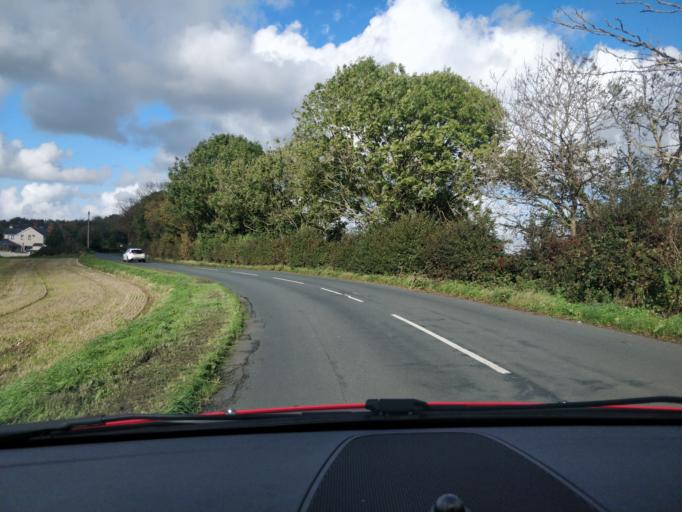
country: GB
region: England
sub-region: Lancashire
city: Parbold
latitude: 53.6045
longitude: -2.7930
